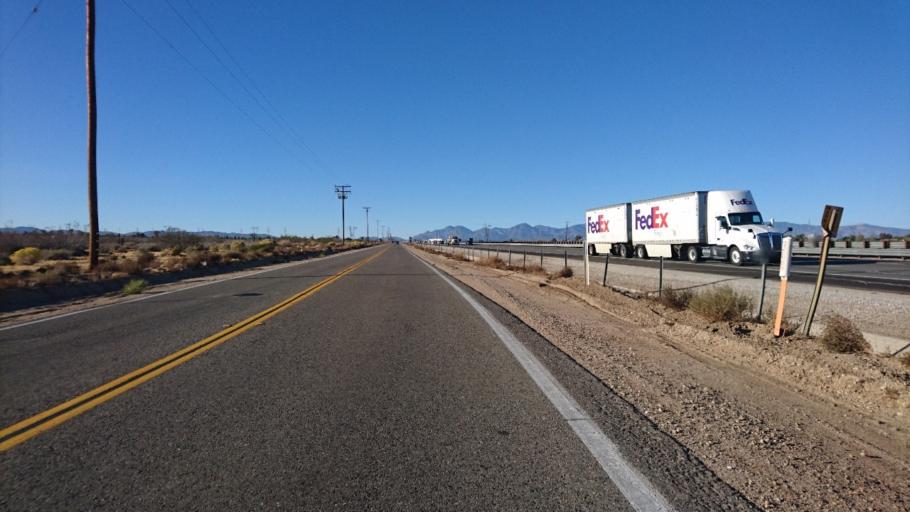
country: US
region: California
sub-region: San Bernardino County
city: Mountain View Acres
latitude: 34.4538
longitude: -117.3587
